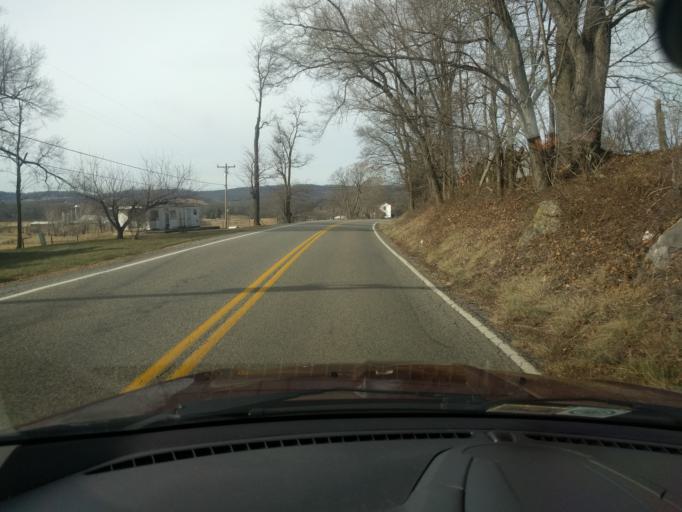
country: US
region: Virginia
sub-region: Augusta County
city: Stuarts Draft
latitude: 38.0415
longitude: -79.0829
